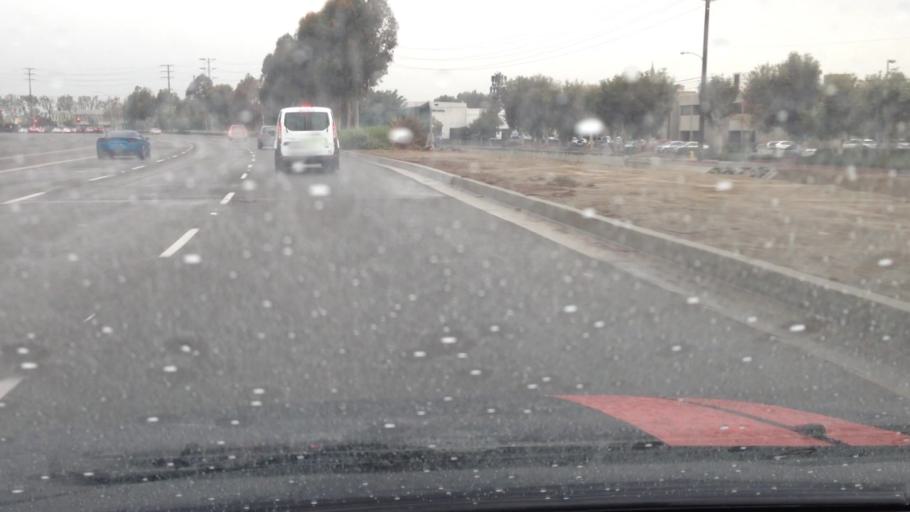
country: US
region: California
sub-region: Orange County
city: Irvine
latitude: 33.6913
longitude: -117.8533
